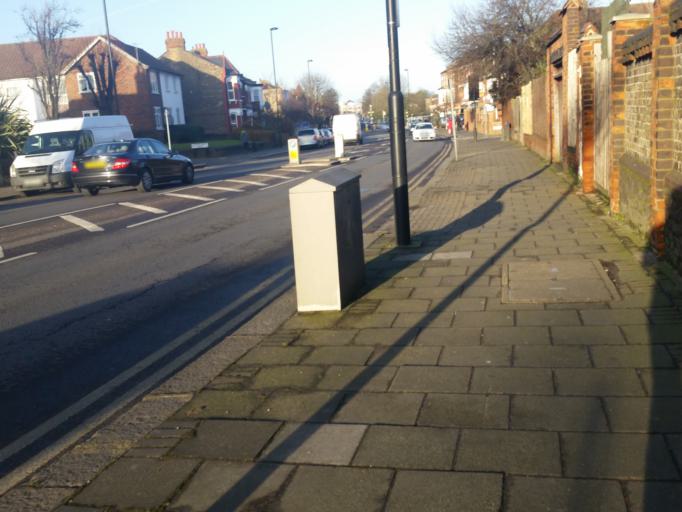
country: GB
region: England
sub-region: Greater London
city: Enfield
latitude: 51.6256
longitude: -0.0995
